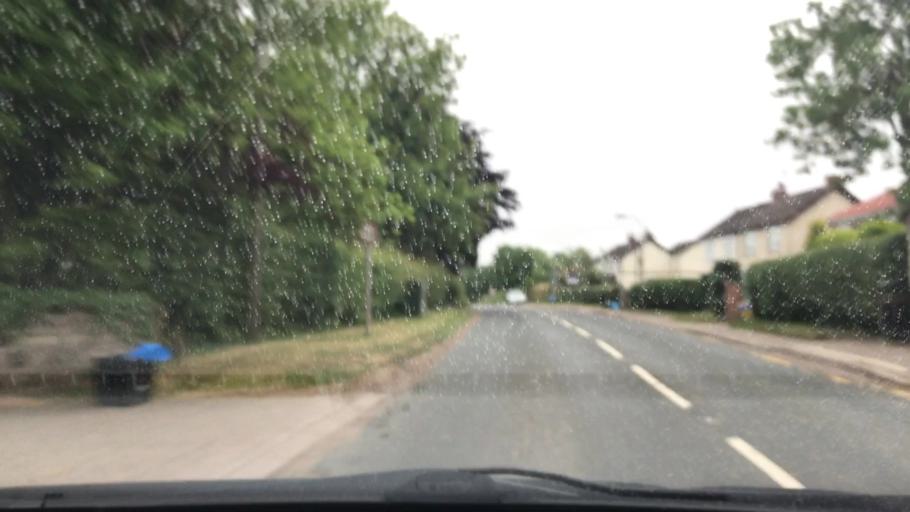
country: GB
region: England
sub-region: City and Borough of Leeds
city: Wetherby
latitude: 53.9593
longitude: -1.4052
